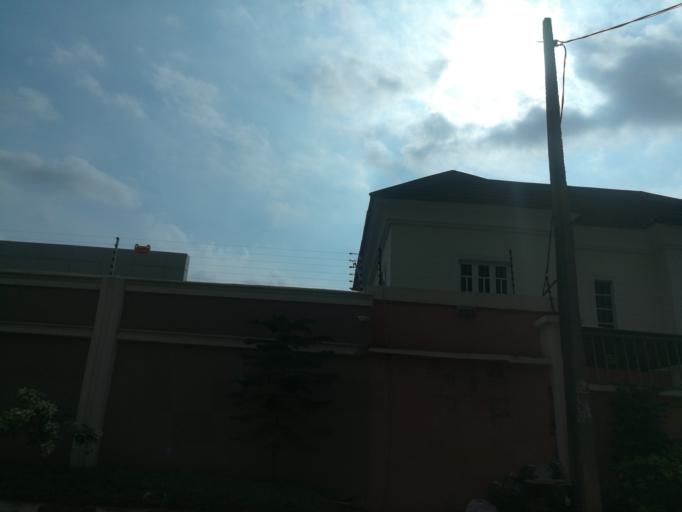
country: NG
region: Lagos
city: Oshodi
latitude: 6.5738
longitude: 3.3575
